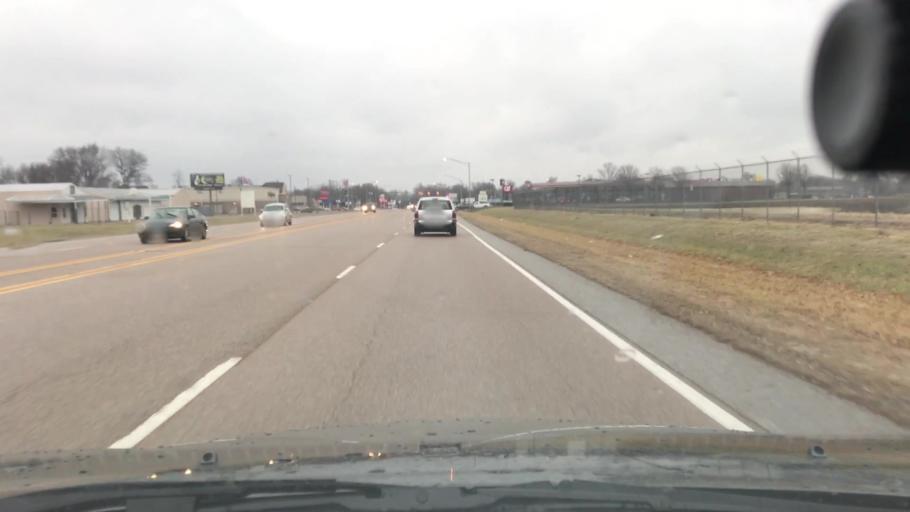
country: US
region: Illinois
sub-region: Madison County
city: Bethalto
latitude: 38.8980
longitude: -90.0592
